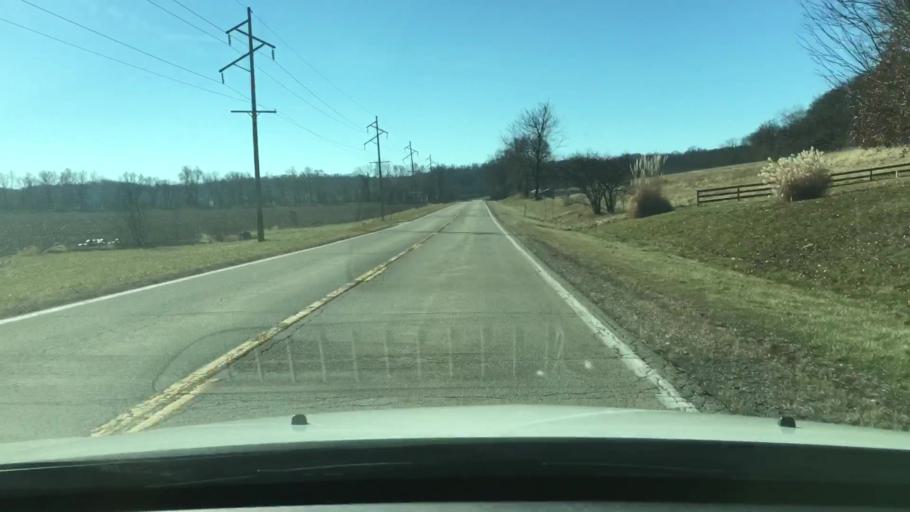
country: US
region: Illinois
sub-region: Mason County
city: Havana
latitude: 40.2303
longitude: -90.1996
